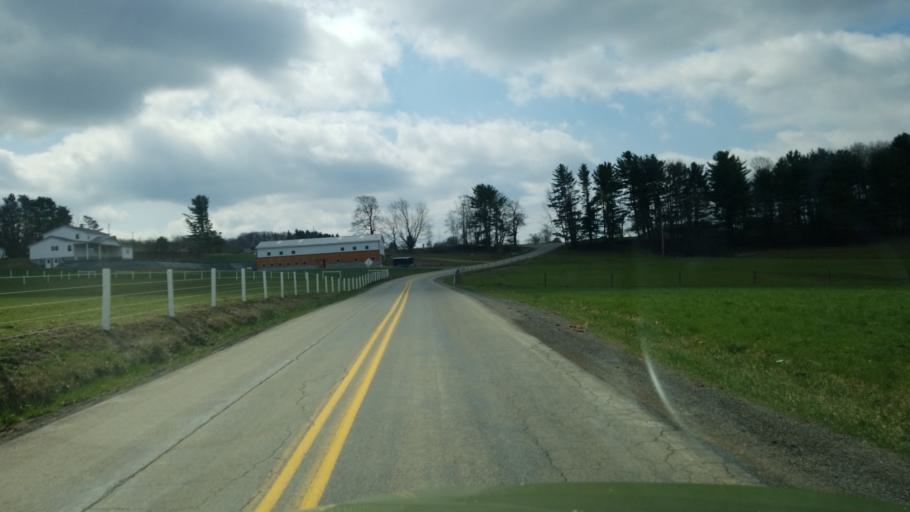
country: US
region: Pennsylvania
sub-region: Jefferson County
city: Brockway
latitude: 41.2774
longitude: -78.8426
